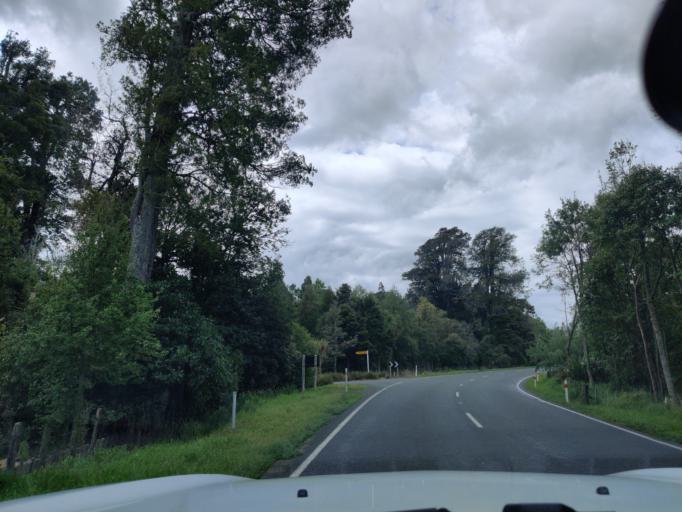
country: NZ
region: Manawatu-Wanganui
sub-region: Palmerston North City
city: Palmerston North
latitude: -40.2468
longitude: 175.5392
